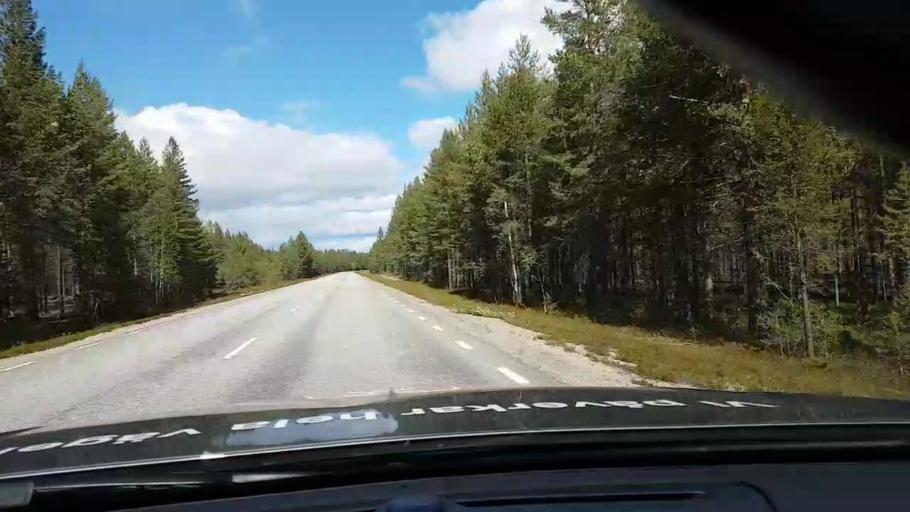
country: SE
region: Vaesternorrland
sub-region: OErnskoeldsviks Kommun
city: Bredbyn
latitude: 63.6180
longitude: 17.9071
